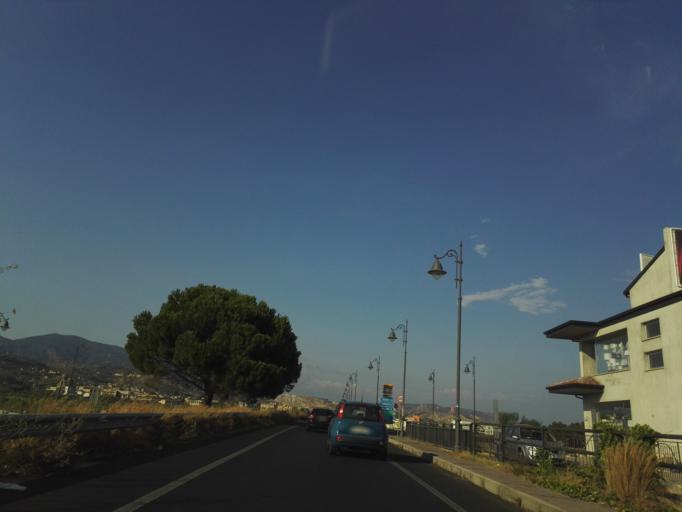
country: IT
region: Calabria
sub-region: Provincia di Reggio Calabria
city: Marina di Gioiosa Ionica
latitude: 38.2942
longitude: 16.3217
